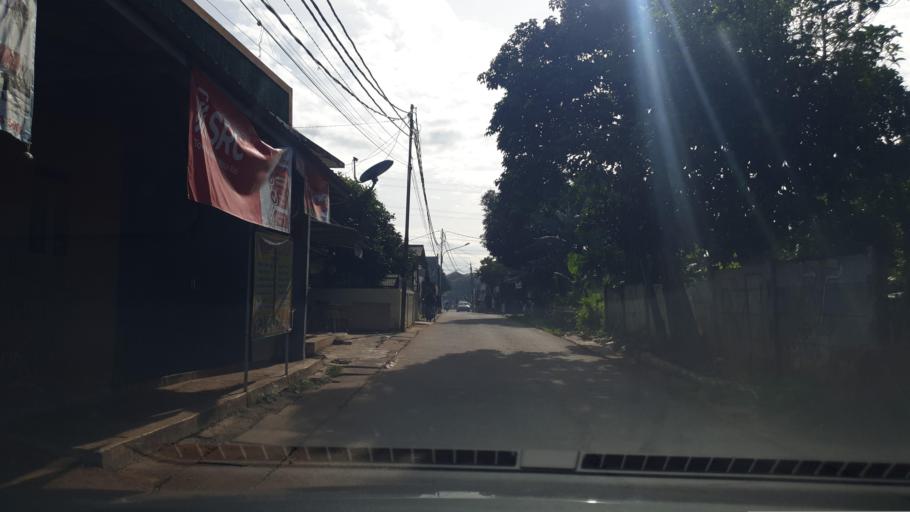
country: ID
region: West Java
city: Sawangan
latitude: -6.3583
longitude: 106.7835
